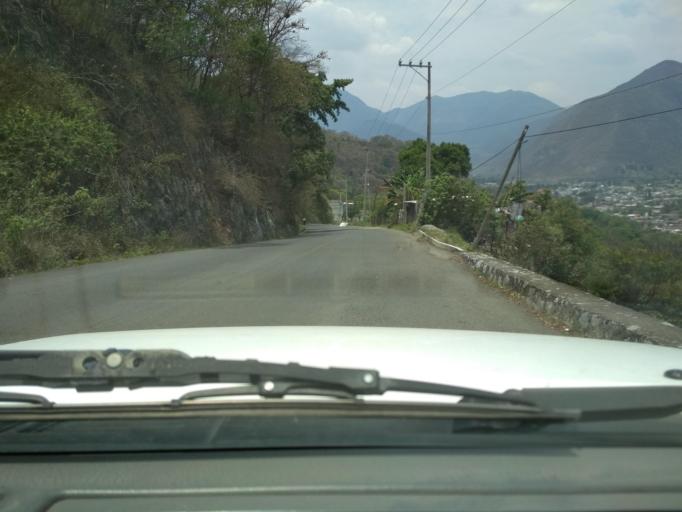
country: MX
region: Veracruz
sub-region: Camerino Z. Mendoza
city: La Cuesta
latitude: 18.7944
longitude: -97.1752
